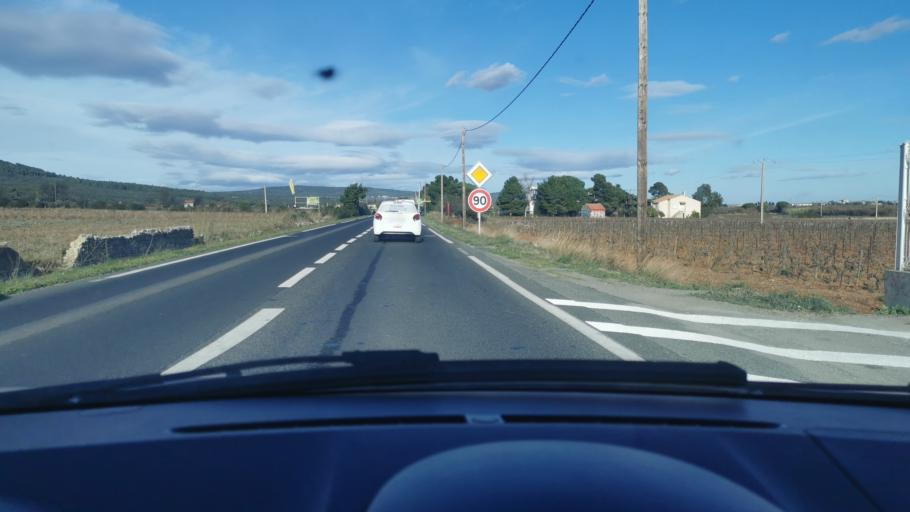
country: FR
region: Languedoc-Roussillon
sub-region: Departement de l'Herault
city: Vic-la-Gardiole
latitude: 43.4755
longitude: 3.7709
